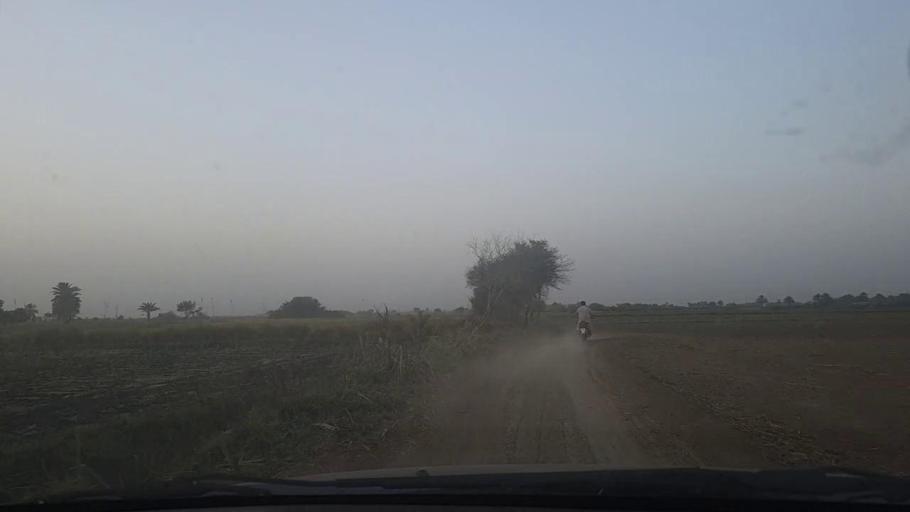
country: PK
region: Sindh
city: Mirpur Sakro
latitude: 24.3810
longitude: 67.6502
